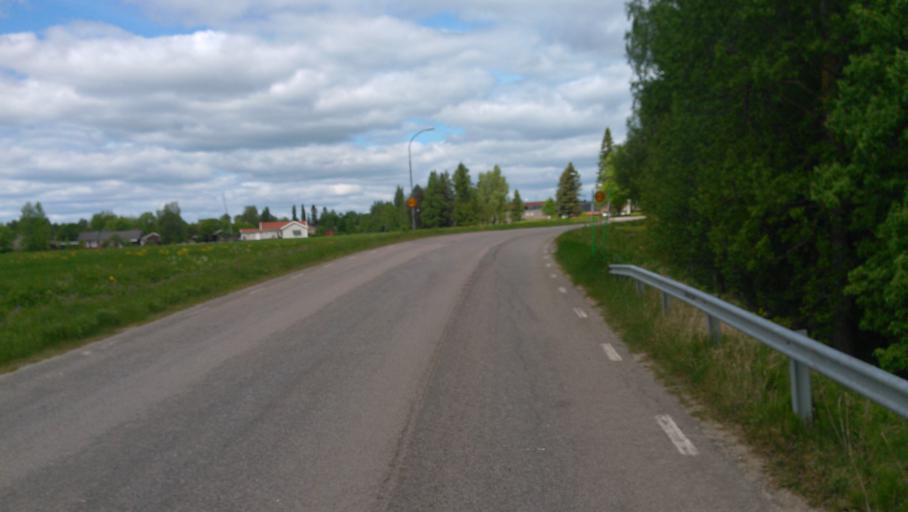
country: SE
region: Vaesterbotten
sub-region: Umea Kommun
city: Roback
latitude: 63.8704
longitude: 20.0662
